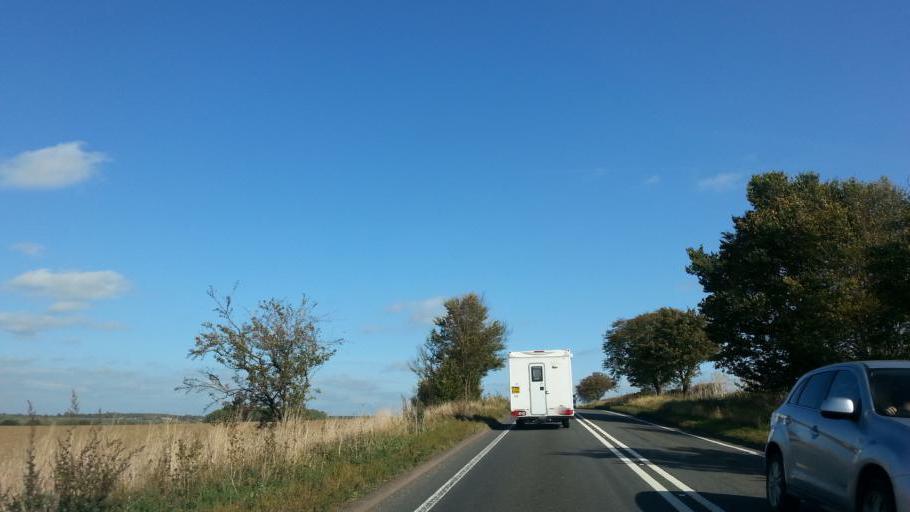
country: GB
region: England
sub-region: Northamptonshire
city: Thrapston
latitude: 52.4085
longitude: -0.5142
